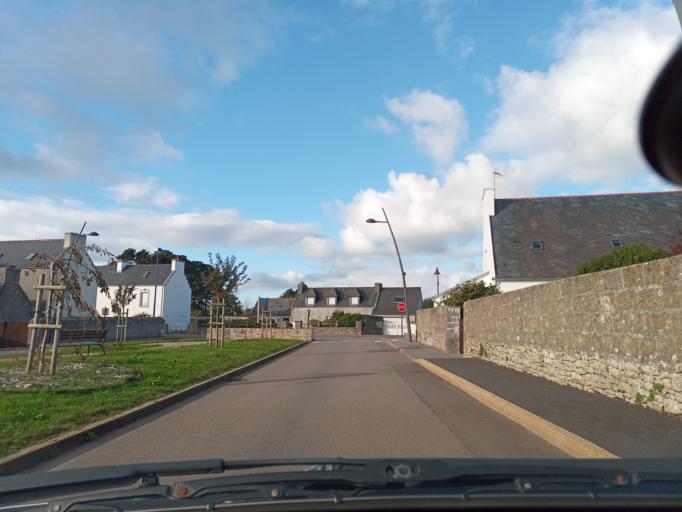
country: FR
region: Brittany
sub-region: Departement du Finistere
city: Plouhinec
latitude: 48.0141
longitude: -4.4884
